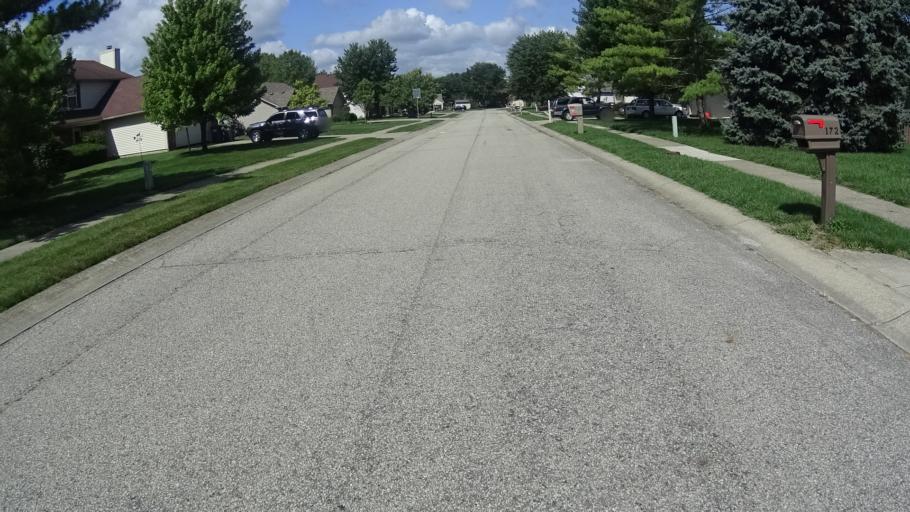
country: US
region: Indiana
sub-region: Madison County
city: Pendleton
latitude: 39.9886
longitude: -85.7458
